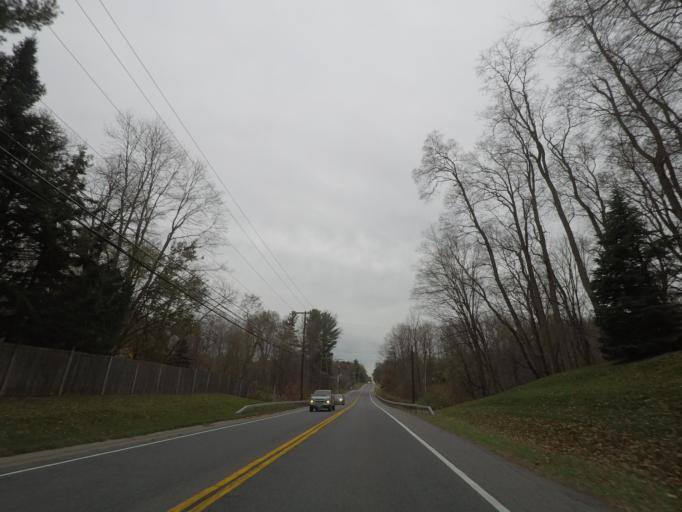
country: US
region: New York
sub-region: Saratoga County
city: Country Knolls
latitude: 42.8836
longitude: -73.8210
